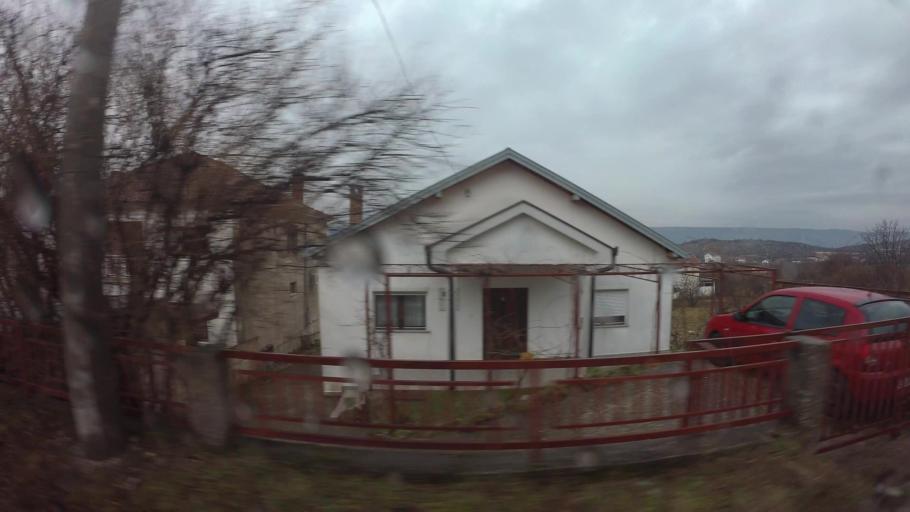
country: BA
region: Federation of Bosnia and Herzegovina
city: Blagaj
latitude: 43.2909
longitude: 17.8595
